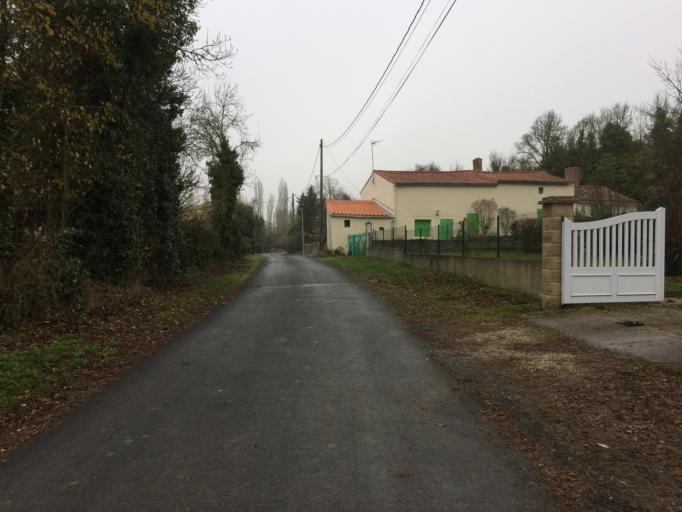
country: FR
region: Pays de la Loire
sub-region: Departement de la Vendee
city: Chaille-les-Marais
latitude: 46.3781
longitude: -1.0222
